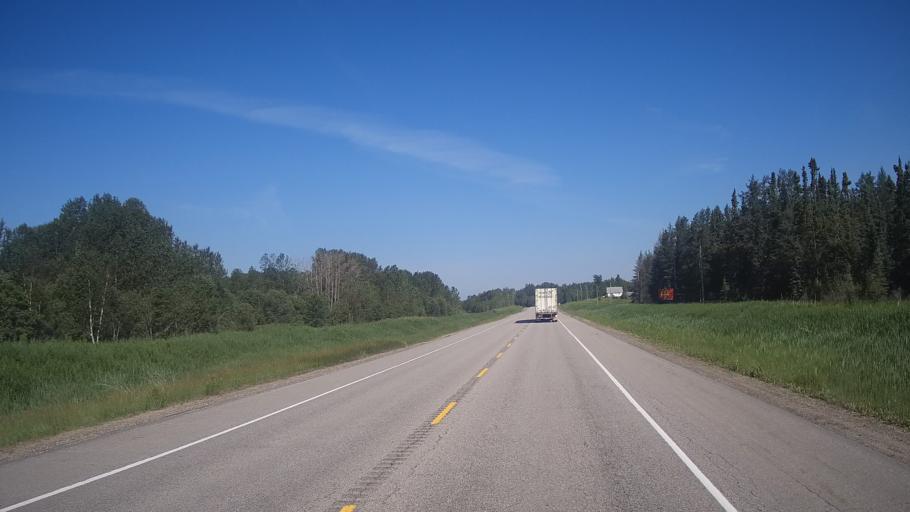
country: CA
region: Ontario
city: Dryden
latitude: 49.6998
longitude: -92.5715
